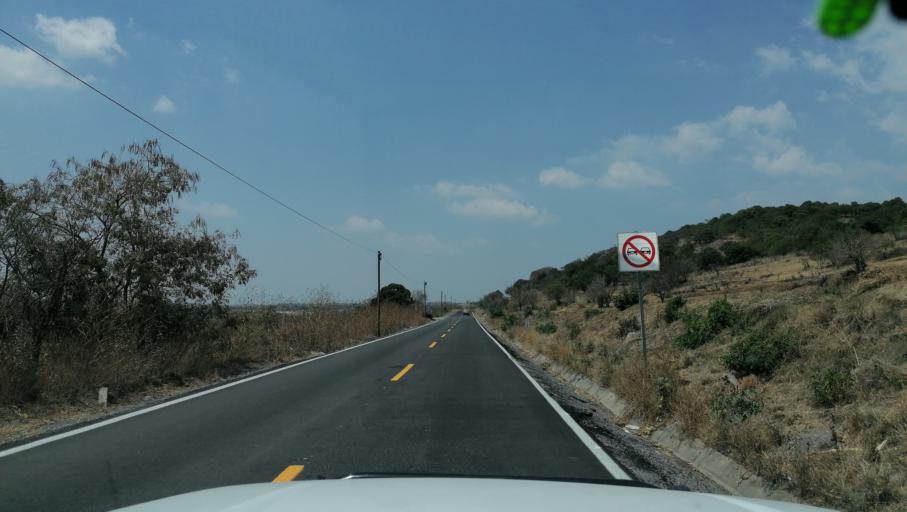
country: MX
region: Puebla
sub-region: Atzitzihuacan
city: Santiago Atzitzihuacan
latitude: 18.8324
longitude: -98.6180
